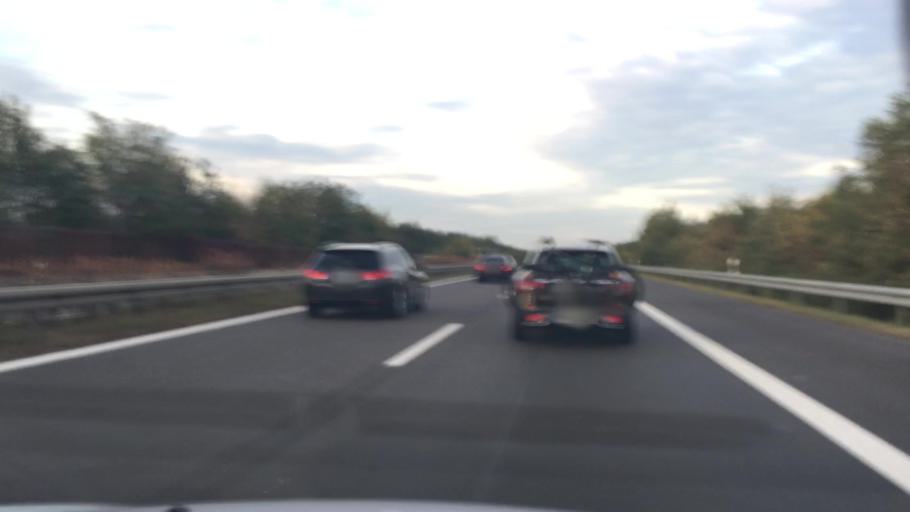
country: DE
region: Brandenburg
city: Schwarzheide
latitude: 51.4737
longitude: 13.8689
